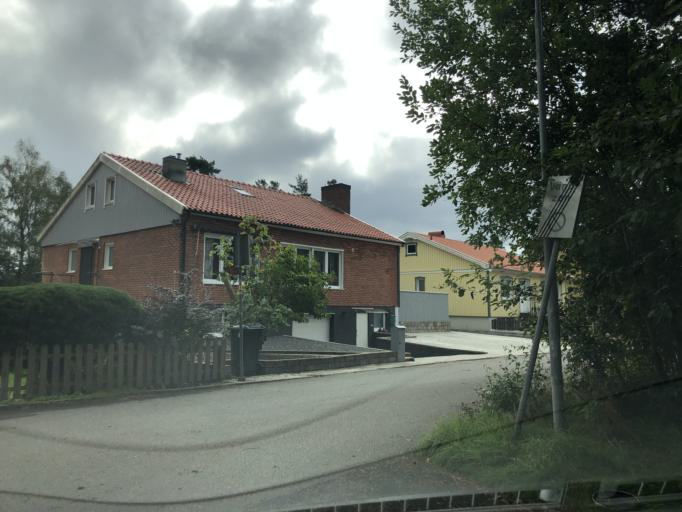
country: SE
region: Vaestra Goetaland
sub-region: Goteborg
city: Majorna
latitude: 57.7442
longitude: 11.9133
